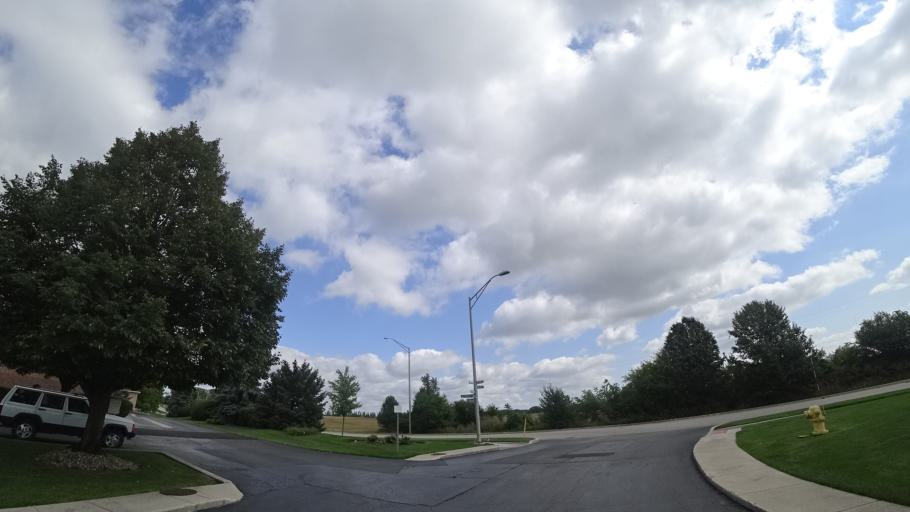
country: US
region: Illinois
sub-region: Will County
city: Mokena
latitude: 41.5586
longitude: -87.8711
